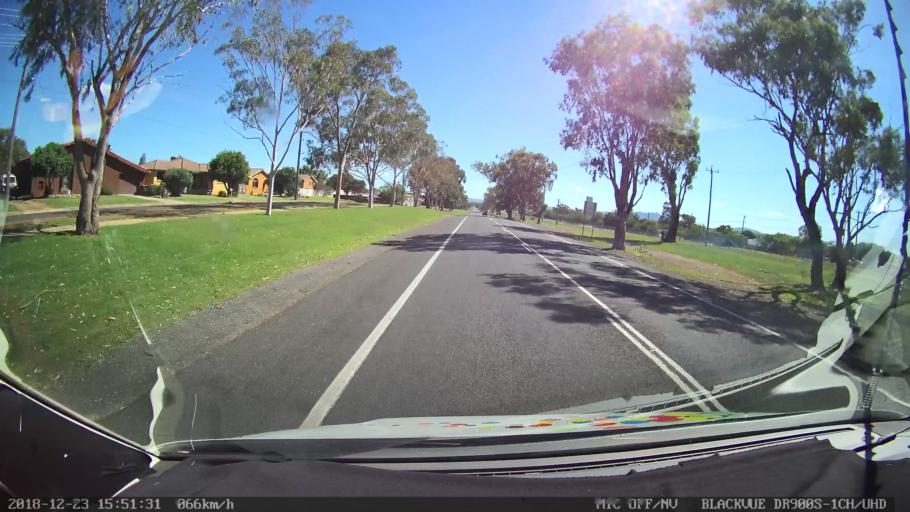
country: AU
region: New South Wales
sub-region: Tamworth Municipality
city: South Tamworth
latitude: -31.1134
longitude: 150.8955
